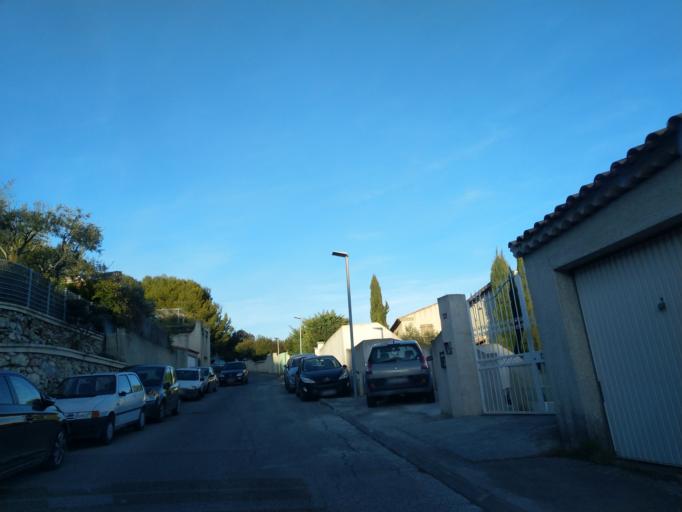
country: FR
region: Provence-Alpes-Cote d'Azur
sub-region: Departement des Bouches-du-Rhone
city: Plan-de-Cuques
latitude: 43.3569
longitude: 5.4630
